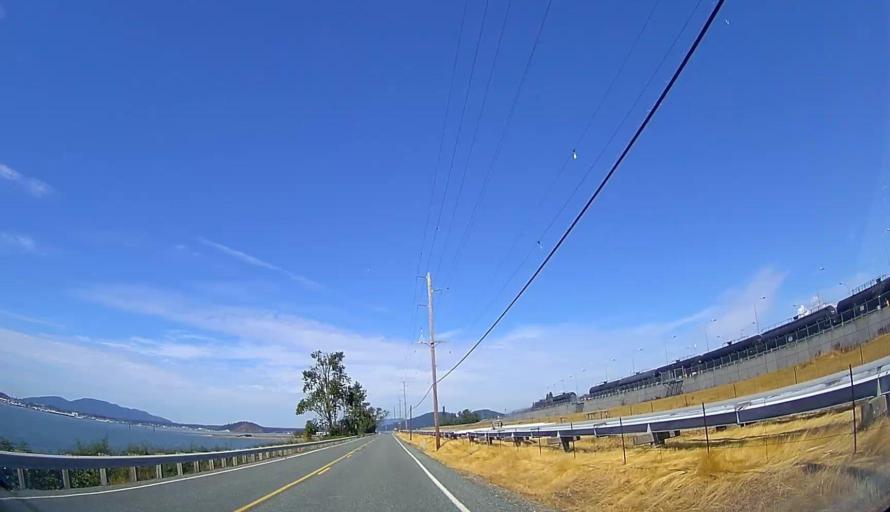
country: US
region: Washington
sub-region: Skagit County
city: Anacortes
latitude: 48.4838
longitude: -122.5742
